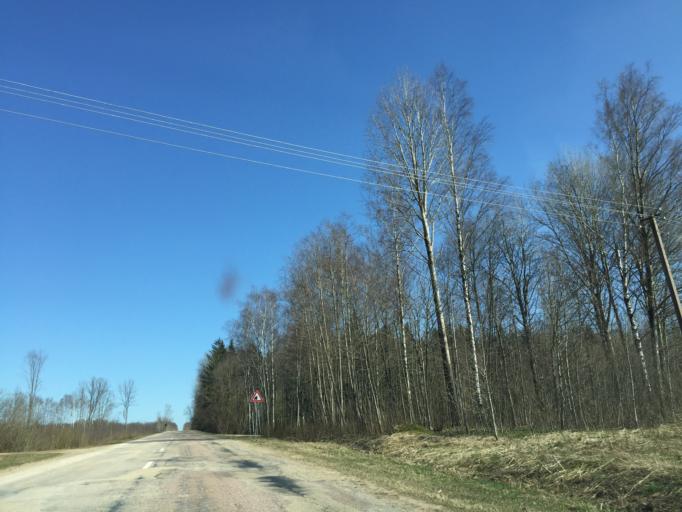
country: LV
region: Malpils
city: Malpils
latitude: 57.0241
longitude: 24.9651
